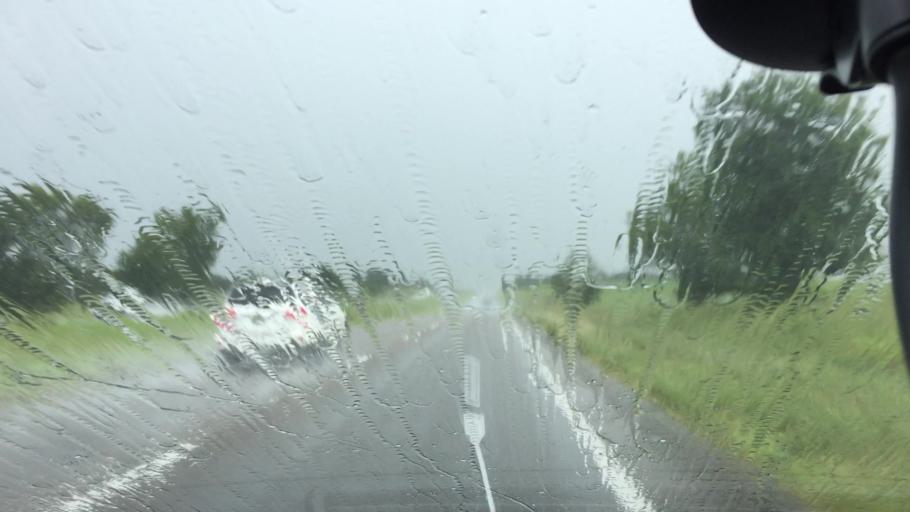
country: US
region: Alabama
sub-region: Montgomery County
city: Pike Road
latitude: 32.2226
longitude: -86.1181
